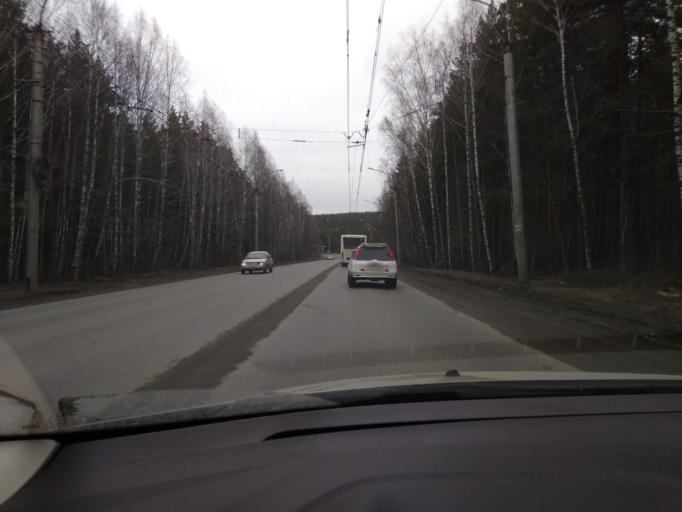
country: RU
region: Chelyabinsk
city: Turgoyak
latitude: 55.1257
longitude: 60.1341
